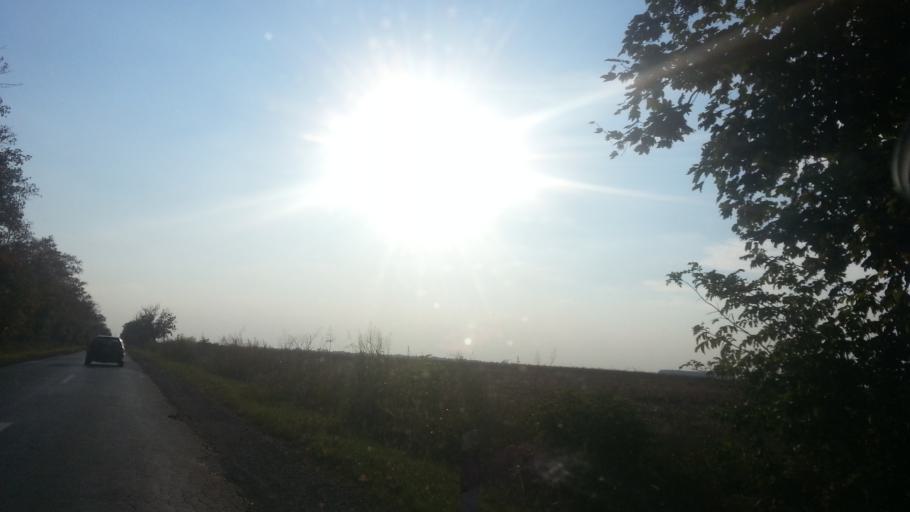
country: RS
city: Novi Karlovci
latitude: 45.0965
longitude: 20.2004
